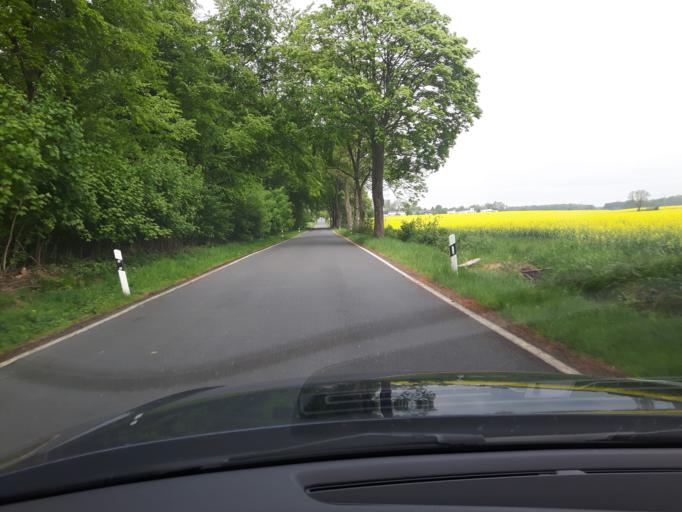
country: DE
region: Mecklenburg-Vorpommern
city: Tribsees
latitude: 54.1821
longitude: 12.7401
